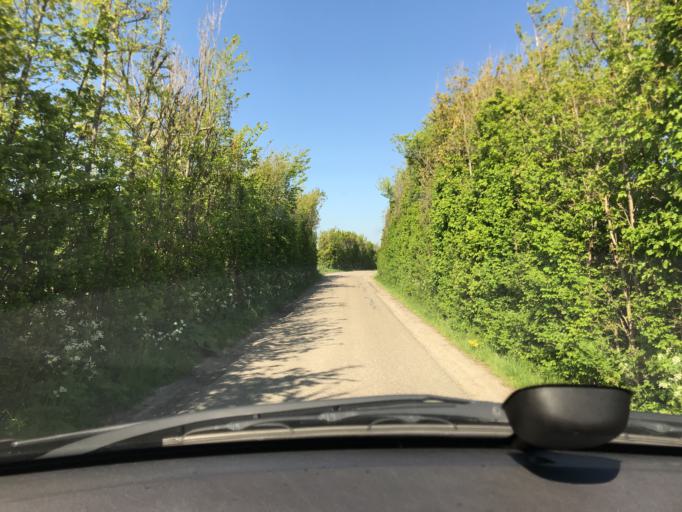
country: NL
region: Zeeland
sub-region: Gemeente Vlissingen
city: Vlissingen
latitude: 51.5143
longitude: 3.4777
